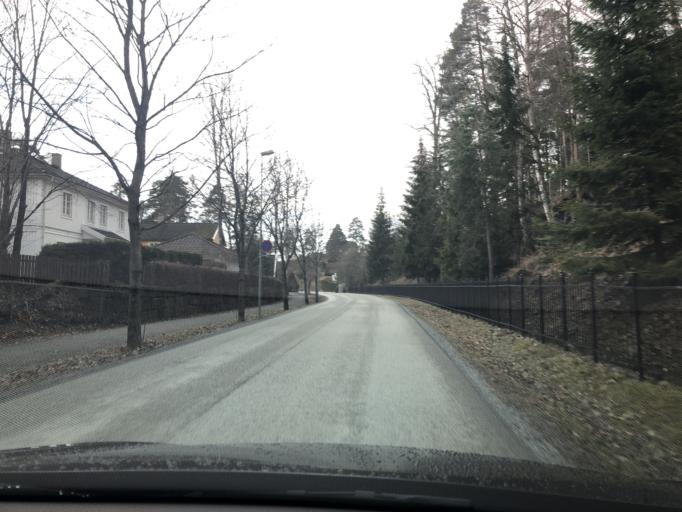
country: NO
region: Akershus
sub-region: Baerum
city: Sandvika
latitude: 59.8617
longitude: 10.5148
